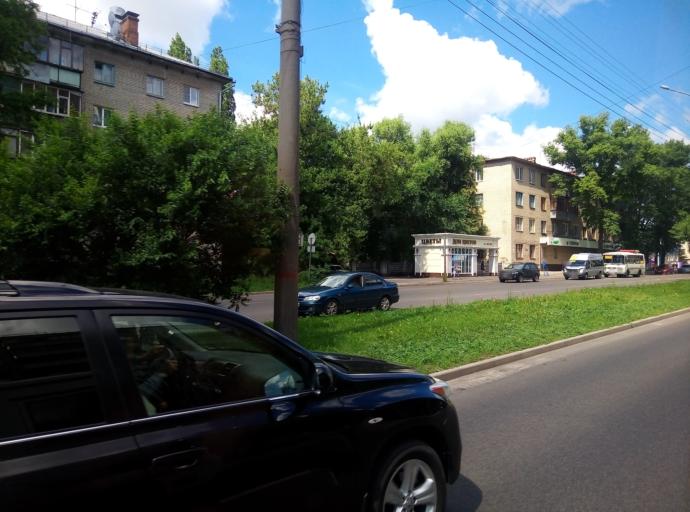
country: RU
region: Kursk
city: Kursk
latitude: 51.7224
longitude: 36.1648
